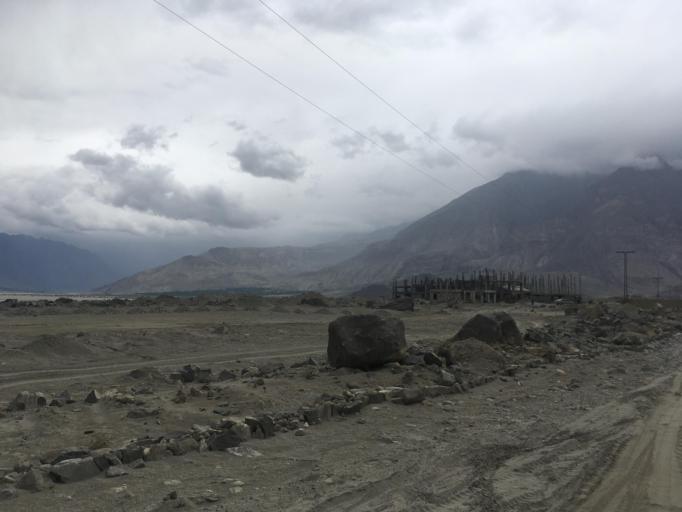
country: PK
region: Gilgit-Baltistan
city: Skardu
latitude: 35.3213
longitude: 75.6559
